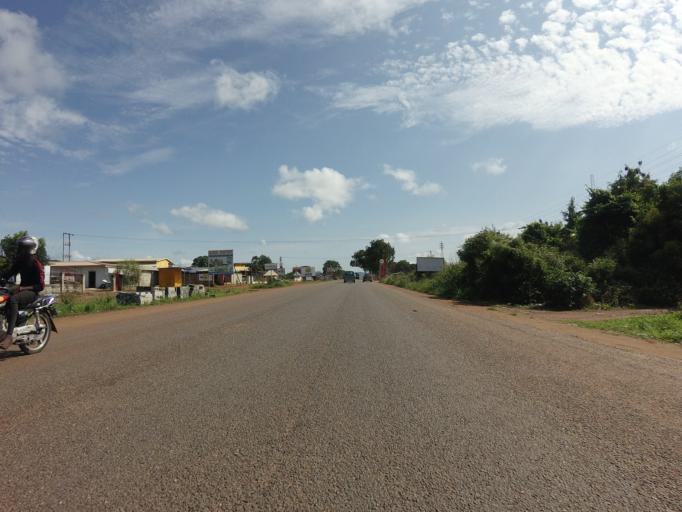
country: GH
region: Eastern
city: Aburi
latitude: 5.7954
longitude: -0.1285
